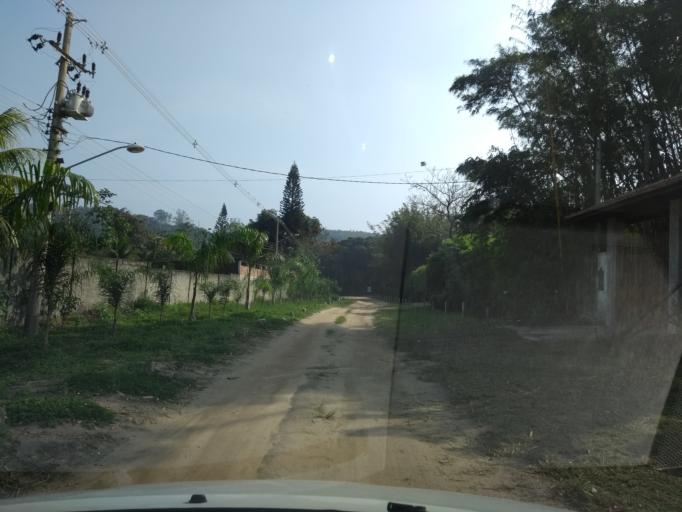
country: BR
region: Rio de Janeiro
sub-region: Itaguai
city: Itaguai
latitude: -22.9660
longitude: -43.6382
